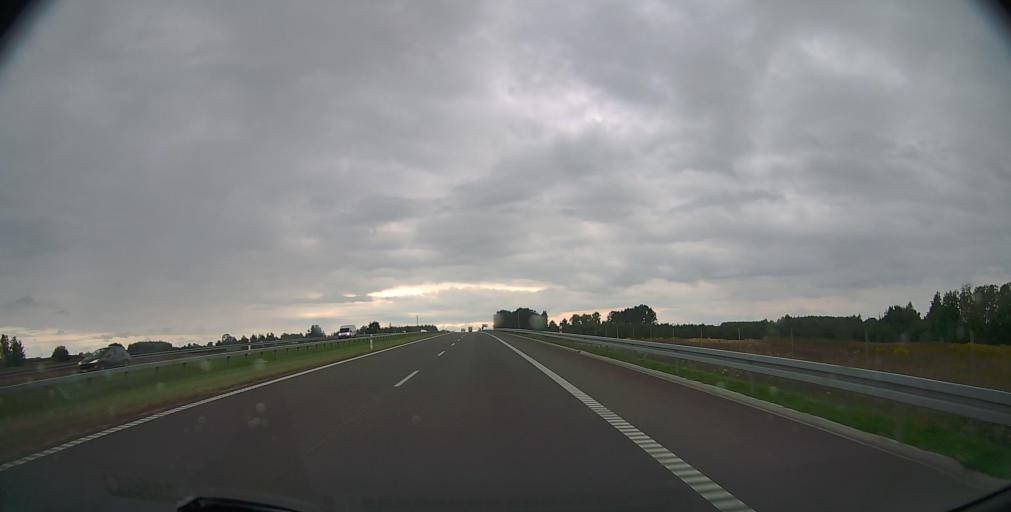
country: PL
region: Masovian Voivodeship
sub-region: Powiat radomski
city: Zakrzew
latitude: 51.4673
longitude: 21.0492
